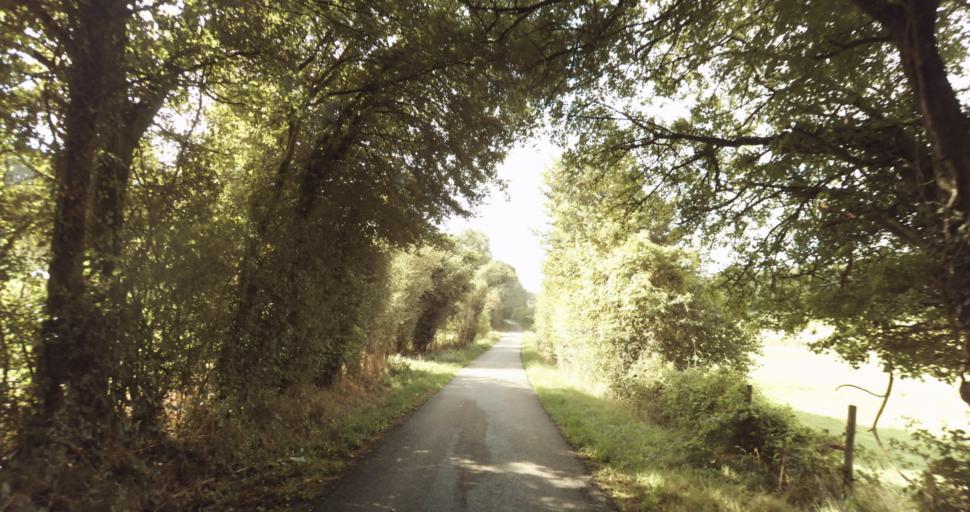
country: FR
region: Lower Normandy
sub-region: Departement de l'Orne
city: Gace
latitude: 48.8014
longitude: 0.2724
